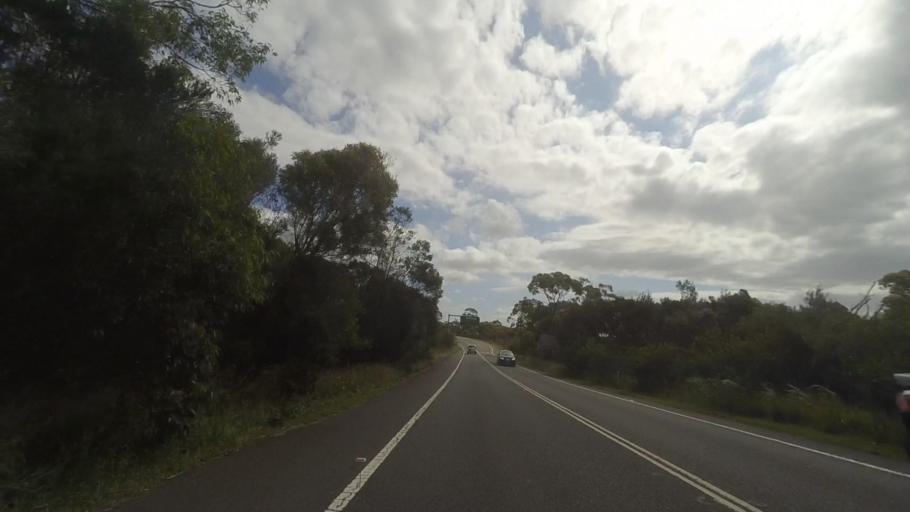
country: AU
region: New South Wales
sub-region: Sutherland Shire
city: Engadine
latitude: -34.0519
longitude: 150.9733
